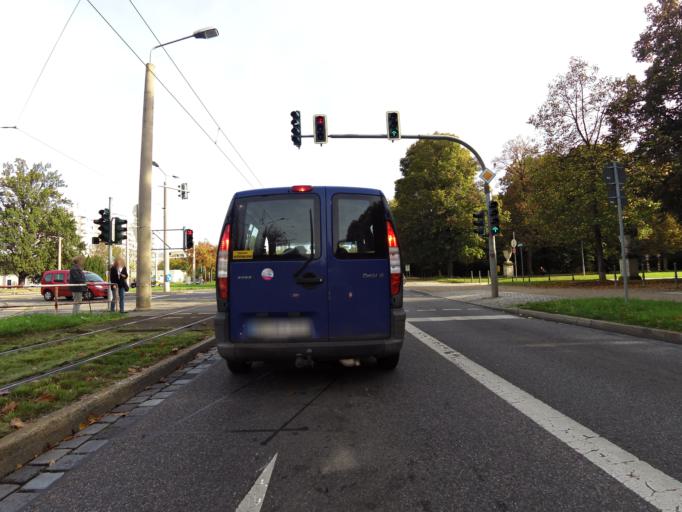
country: DE
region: Saxony
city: Dresden
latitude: 51.0416
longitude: 13.7662
